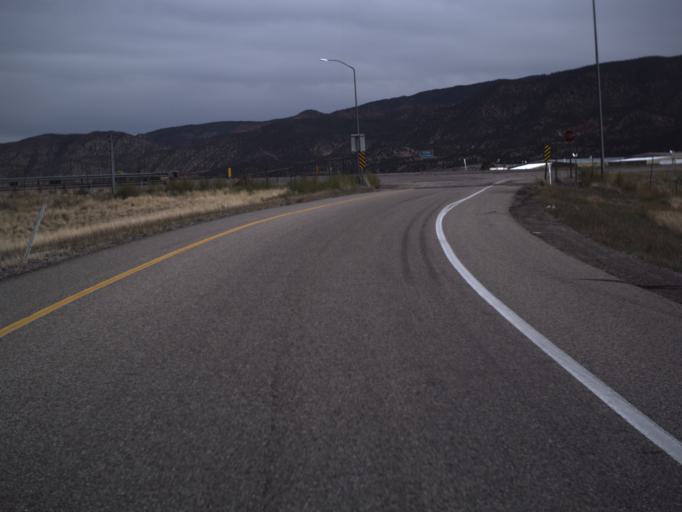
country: US
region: Utah
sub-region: Iron County
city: Parowan
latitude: 37.8572
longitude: -112.8291
